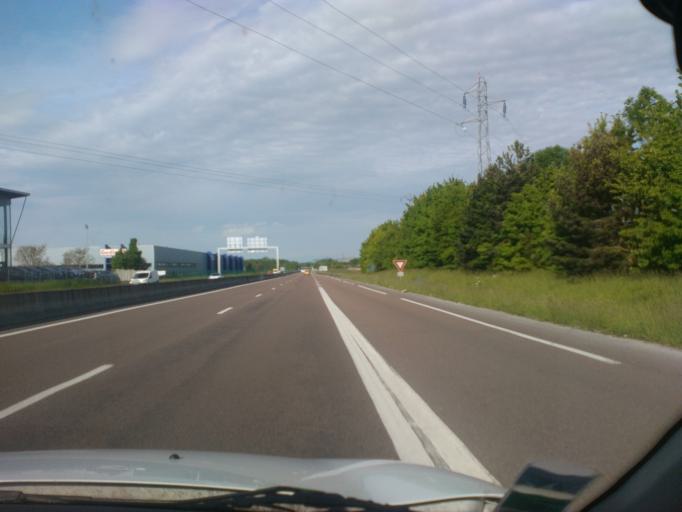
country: FR
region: Champagne-Ardenne
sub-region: Departement de l'Aube
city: Pont-Sainte-Marie
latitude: 48.3341
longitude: 4.0974
